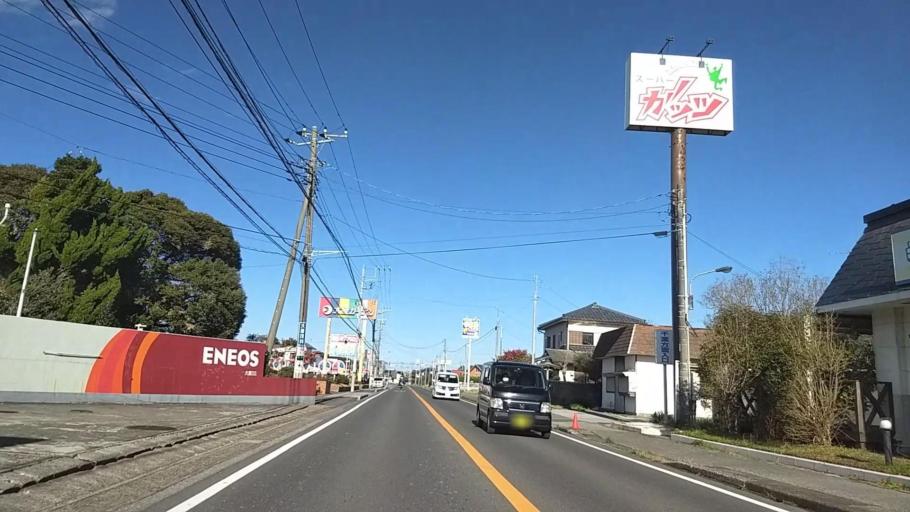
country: JP
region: Chiba
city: Ohara
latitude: 35.2409
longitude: 140.3920
